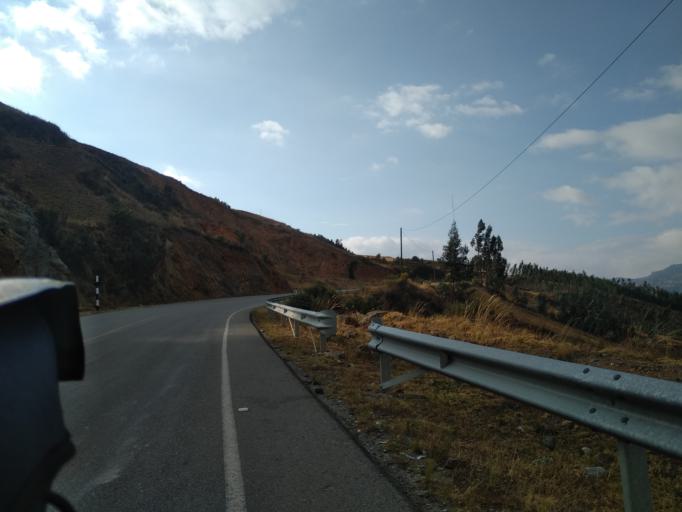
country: PE
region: La Libertad
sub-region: Provincia de Otuzco
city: Agallpampa
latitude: -7.9863
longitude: -78.5350
